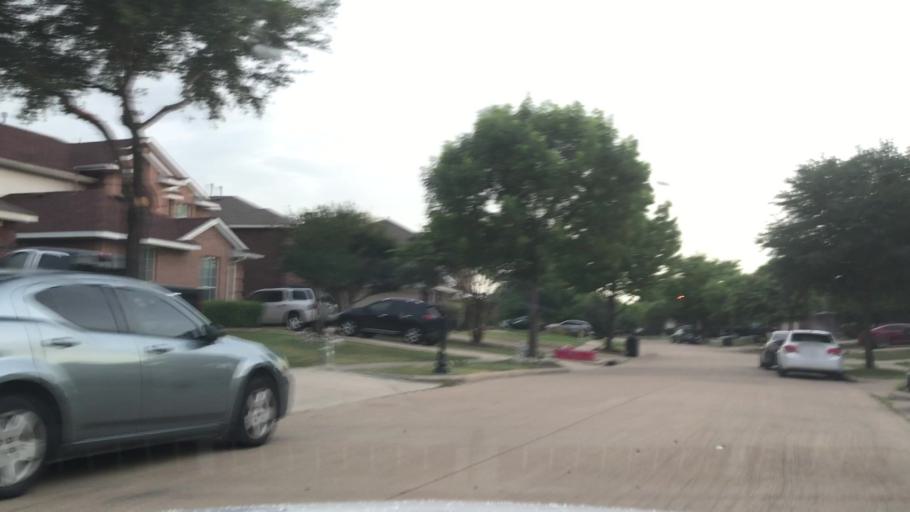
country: US
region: Texas
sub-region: Kaufman County
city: Forney
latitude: 32.7209
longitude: -96.5363
